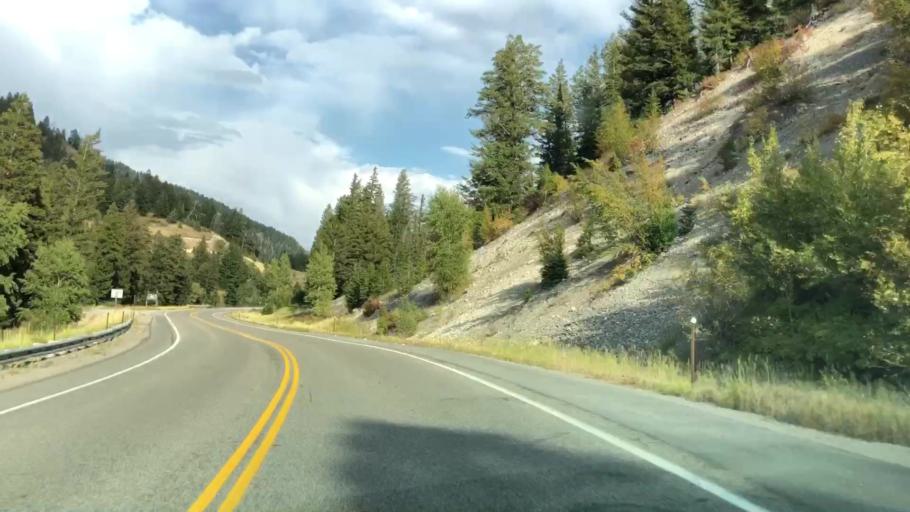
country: US
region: Wyoming
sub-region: Teton County
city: Hoback
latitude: 43.2809
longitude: -110.6162
